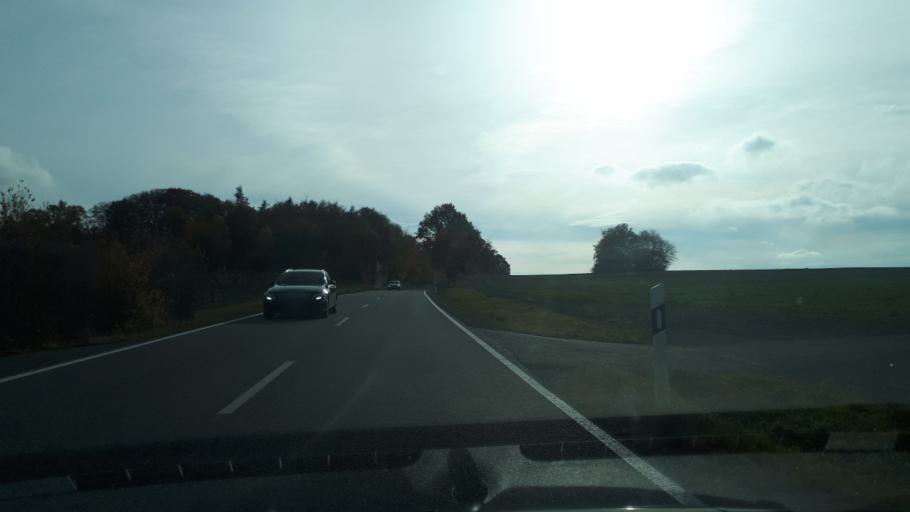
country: DE
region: Rheinland-Pfalz
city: Alflen
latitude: 50.1688
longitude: 7.0402
